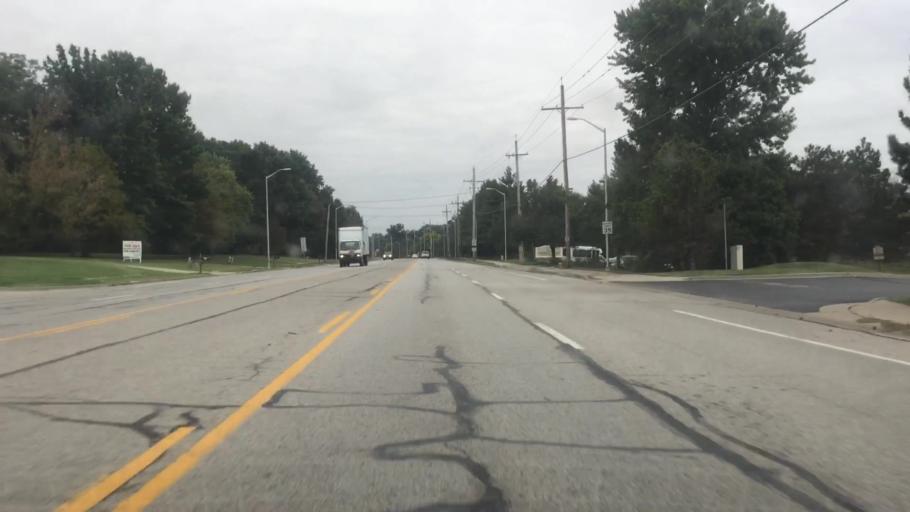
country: US
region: Kansas
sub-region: Johnson County
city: Lenexa
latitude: 38.9988
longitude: -94.7744
